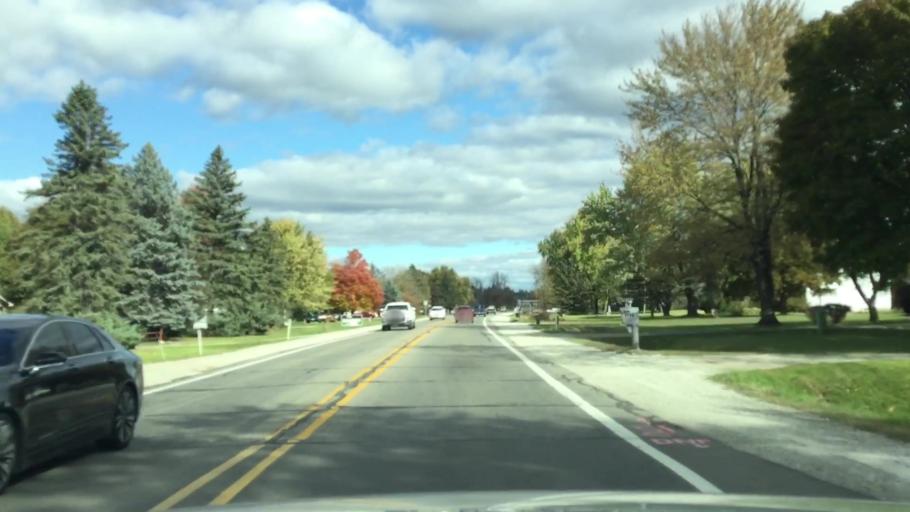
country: US
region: Michigan
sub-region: Lapeer County
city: Lapeer
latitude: 43.0754
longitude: -83.3151
